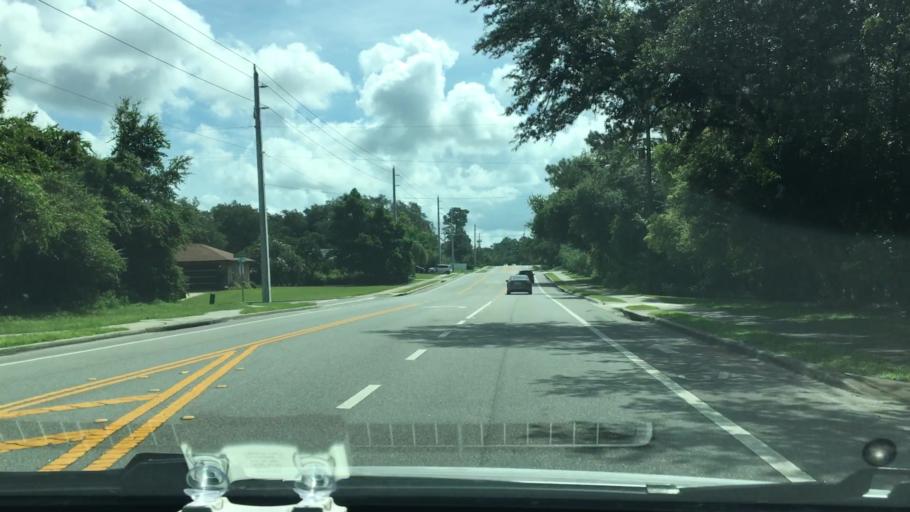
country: US
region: Florida
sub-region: Volusia County
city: Deltona
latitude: 28.8781
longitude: -81.1822
